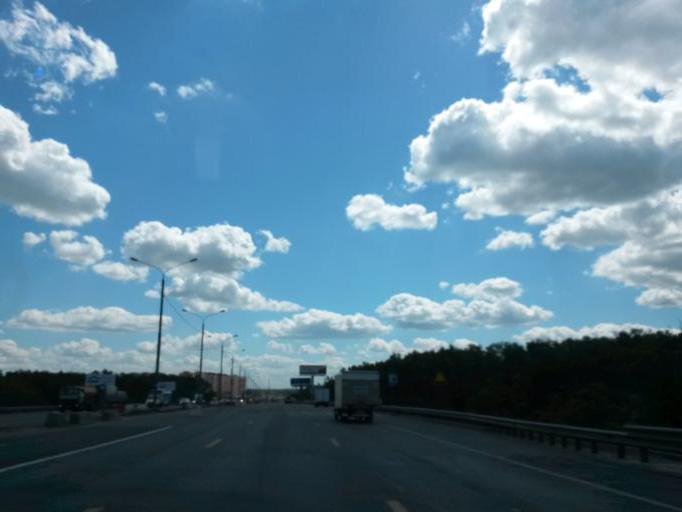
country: RU
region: Moscow
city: Annino
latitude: 55.5442
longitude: 37.6068
